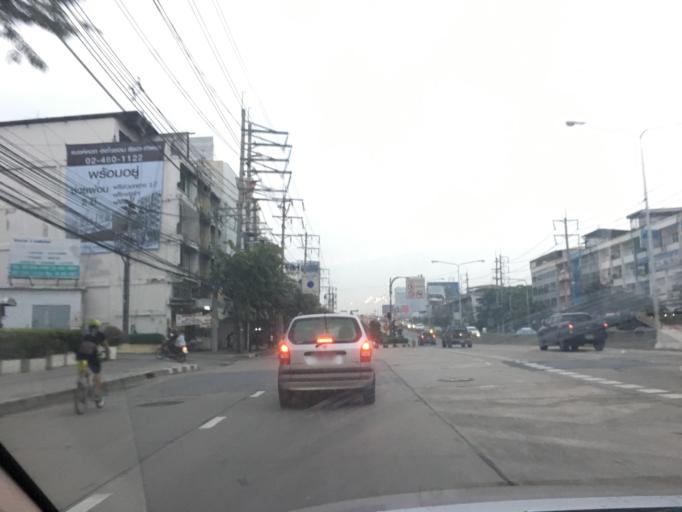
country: TH
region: Bangkok
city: Bang Kho Laem
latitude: 13.6946
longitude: 100.4993
